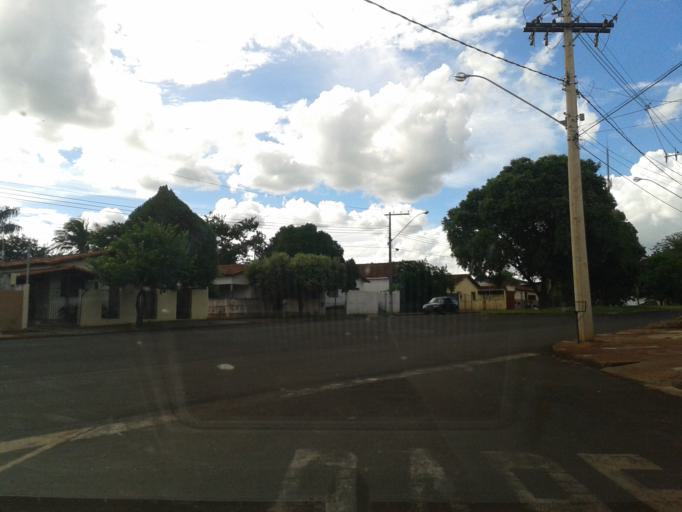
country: BR
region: Minas Gerais
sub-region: Ituiutaba
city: Ituiutaba
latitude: -18.9700
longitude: -49.4516
